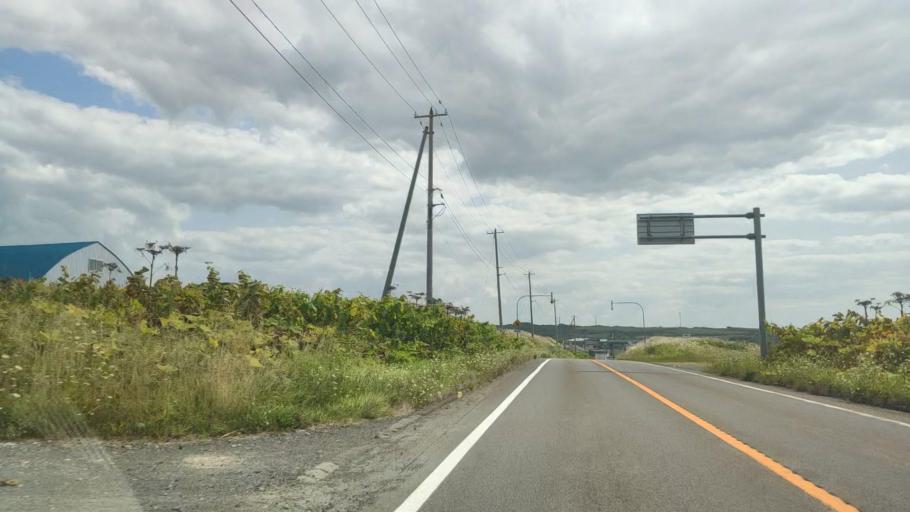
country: JP
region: Hokkaido
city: Rumoi
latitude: 44.5384
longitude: 141.7666
